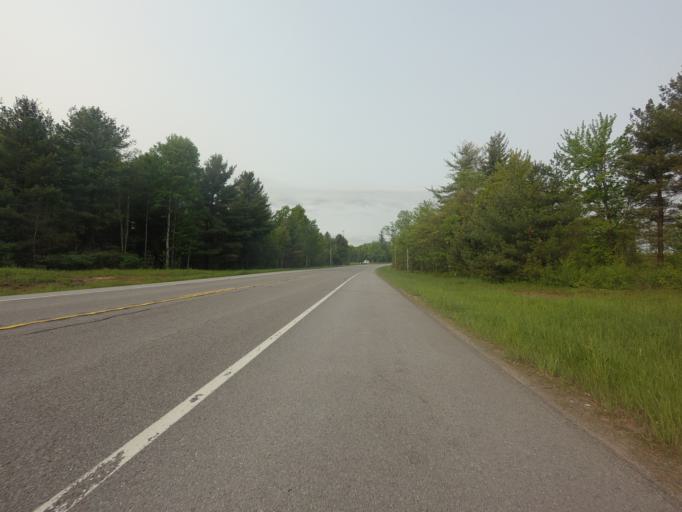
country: US
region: New York
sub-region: Jefferson County
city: Carthage
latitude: 44.0430
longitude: -75.5661
